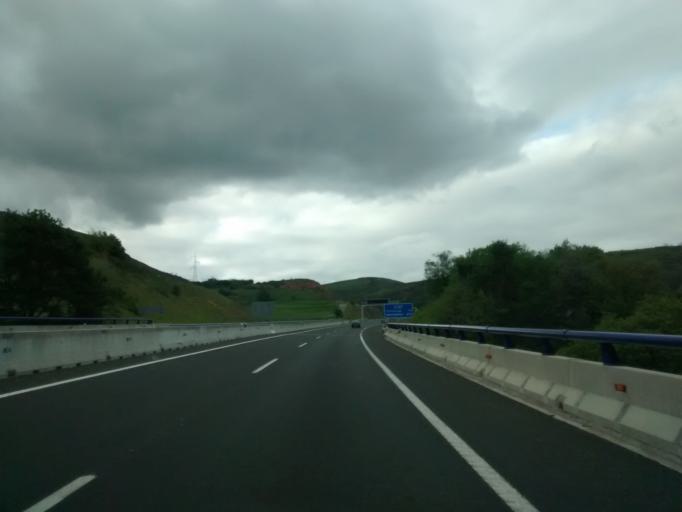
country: ES
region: Cantabria
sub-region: Provincia de Cantabria
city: Arenas de Iguna
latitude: 43.1955
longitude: -4.0713
